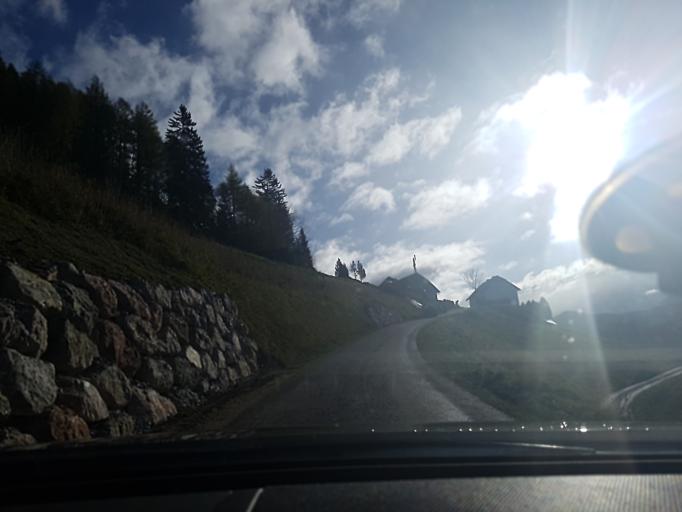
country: AT
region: Styria
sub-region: Politischer Bezirk Murtal
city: Oberzeiring
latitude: 47.2575
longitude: 14.4603
